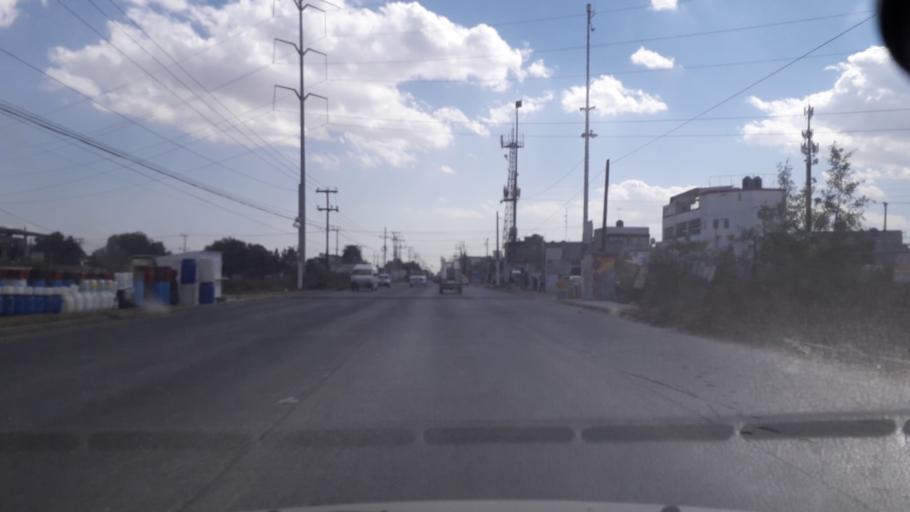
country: MX
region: Mexico
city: Ecatepec
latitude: 19.6379
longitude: -99.0567
